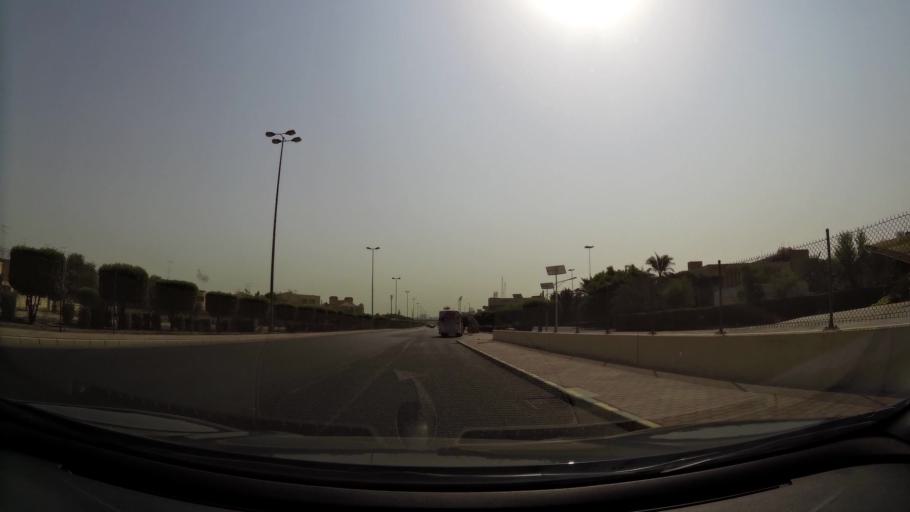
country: KW
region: Al Asimah
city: Ad Dasmah
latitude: 29.3629
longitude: 47.9949
